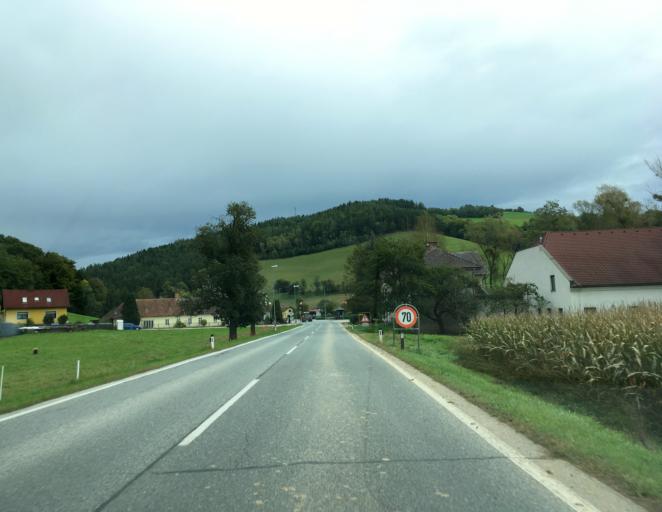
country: AT
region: Lower Austria
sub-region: Politischer Bezirk Wiener Neustadt
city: Bad Schonau
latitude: 47.4983
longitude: 16.2305
